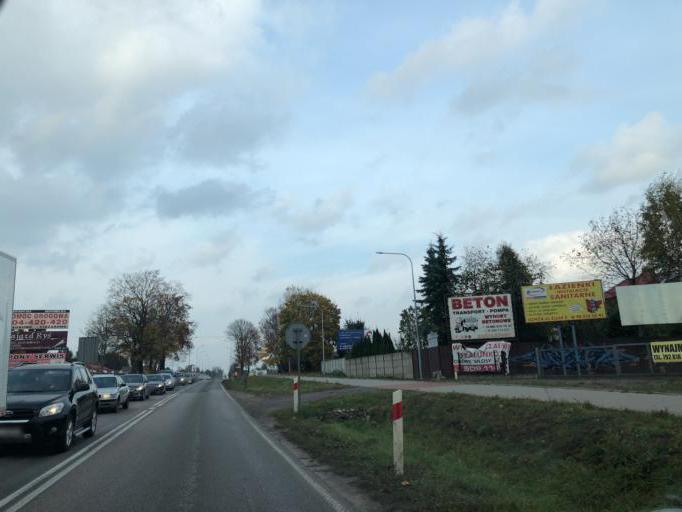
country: PL
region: Podlasie
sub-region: Lomza
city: Lomza
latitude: 53.1452
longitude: 22.0459
